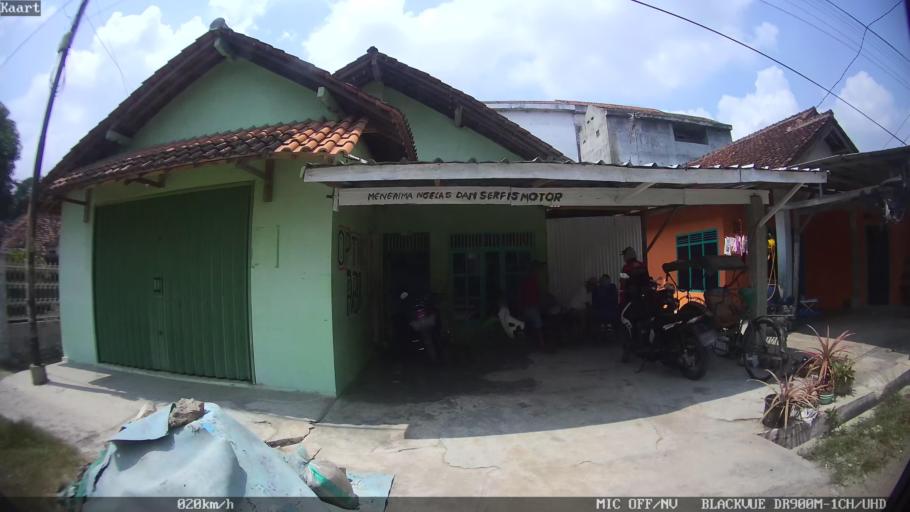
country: ID
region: Lampung
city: Pringsewu
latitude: -5.3582
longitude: 104.9800
